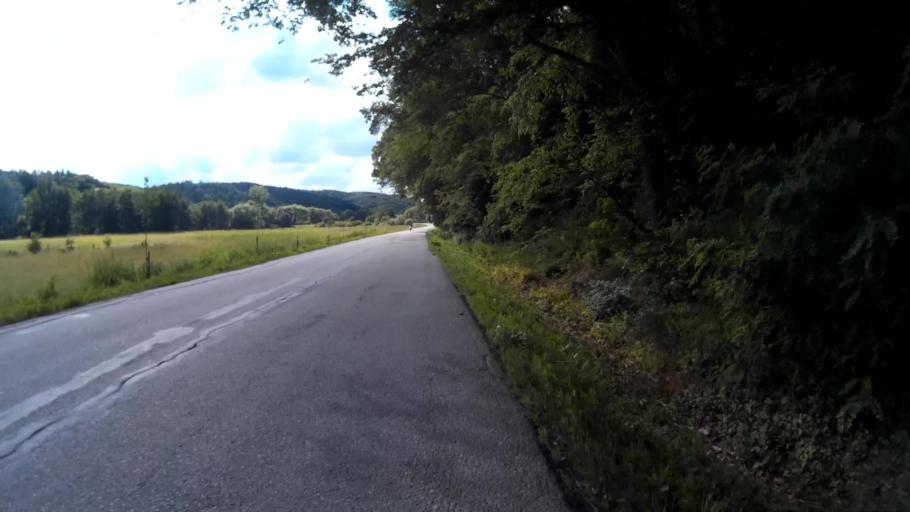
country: CZ
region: South Moravian
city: Strelice
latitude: 49.1529
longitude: 16.4583
